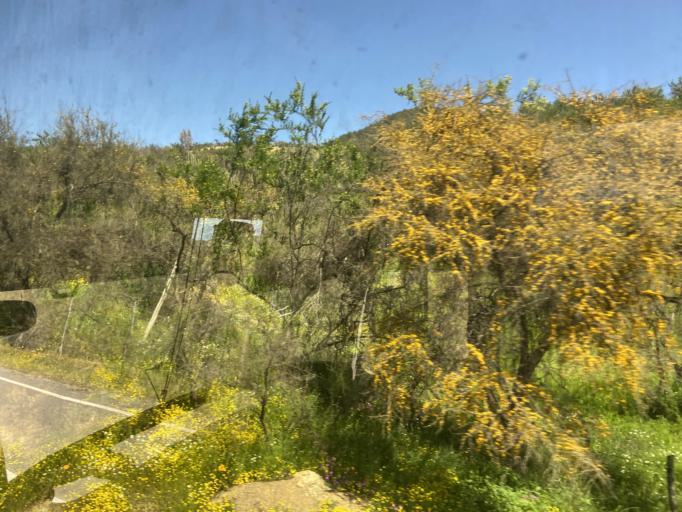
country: CL
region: Valparaiso
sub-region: Provincia de Marga Marga
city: Villa Alemana
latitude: -33.1797
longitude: -71.3064
